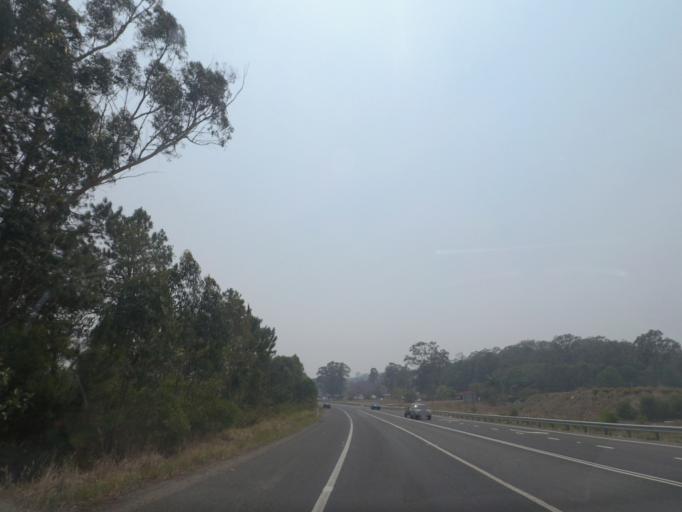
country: AU
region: New South Wales
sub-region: Clarence Valley
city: Maclean
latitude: -29.5633
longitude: 153.1471
